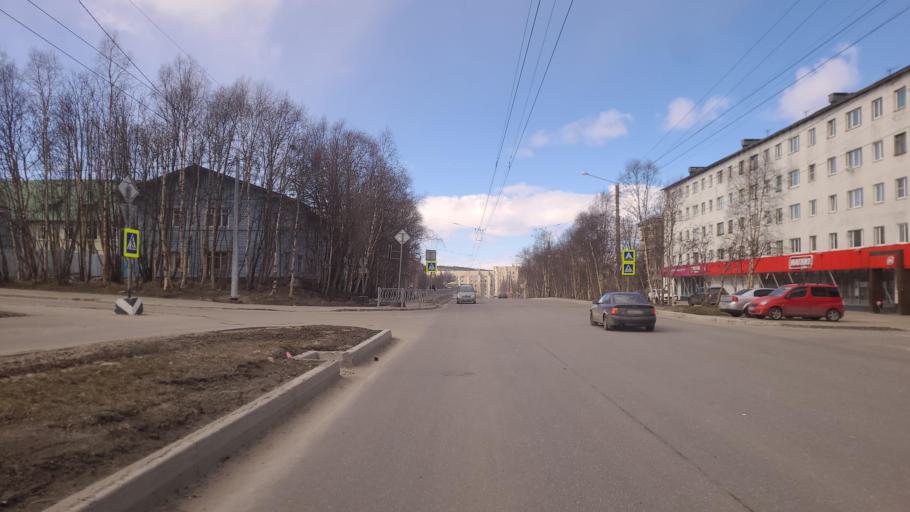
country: RU
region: Murmansk
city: Murmansk
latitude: 68.9528
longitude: 33.0702
